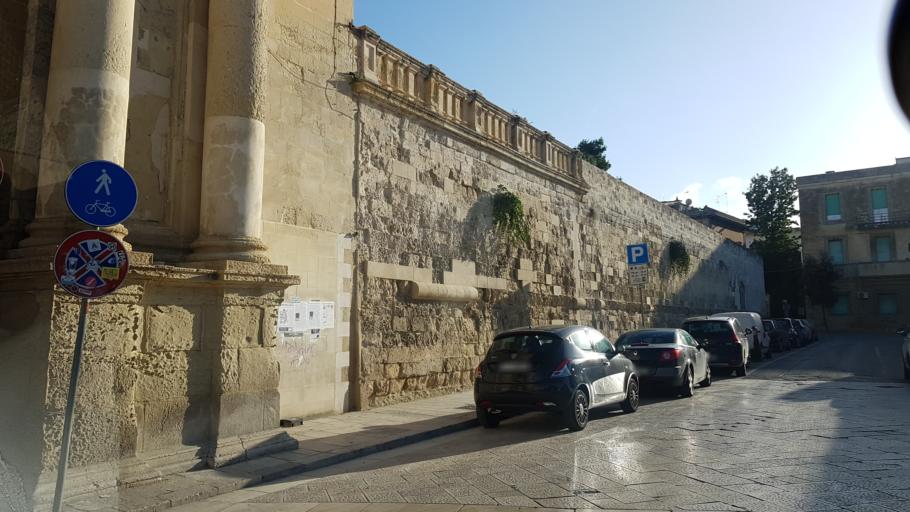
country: IT
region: Apulia
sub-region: Provincia di Lecce
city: Lecce
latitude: 40.3514
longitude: 18.1645
